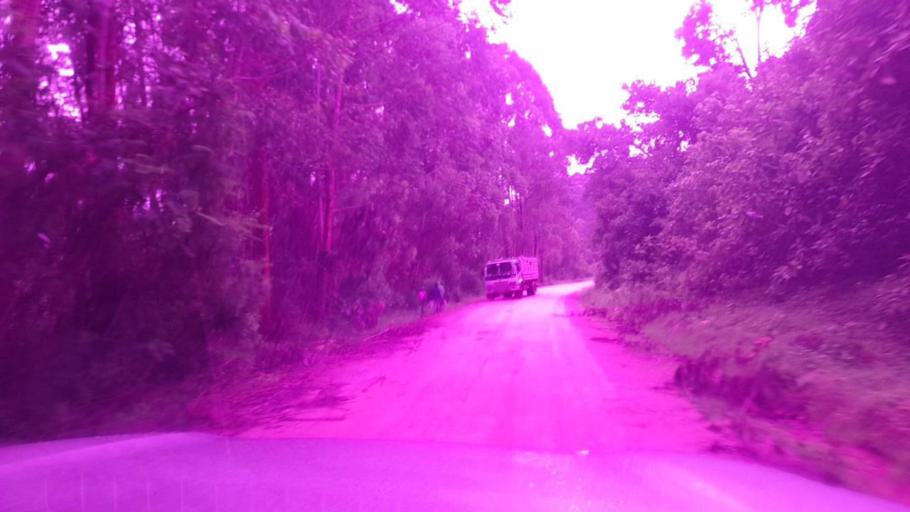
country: ET
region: Southern Nations, Nationalities, and People's Region
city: Bonga
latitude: 7.4586
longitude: 36.1260
